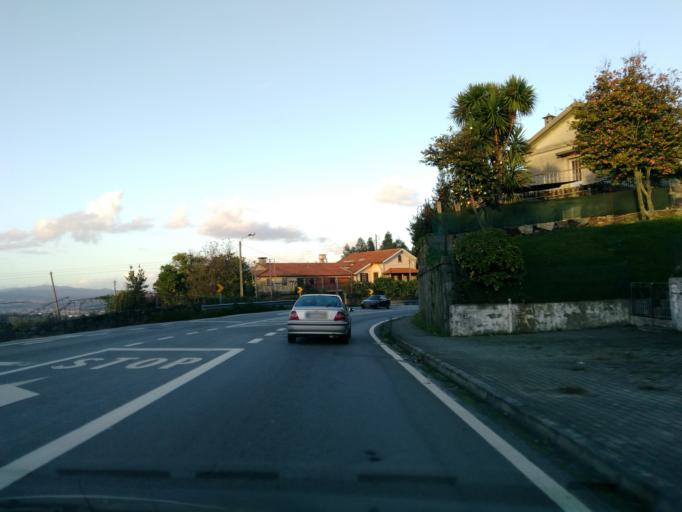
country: PT
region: Braga
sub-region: Braga
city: Braga
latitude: 41.5368
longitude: -8.4537
